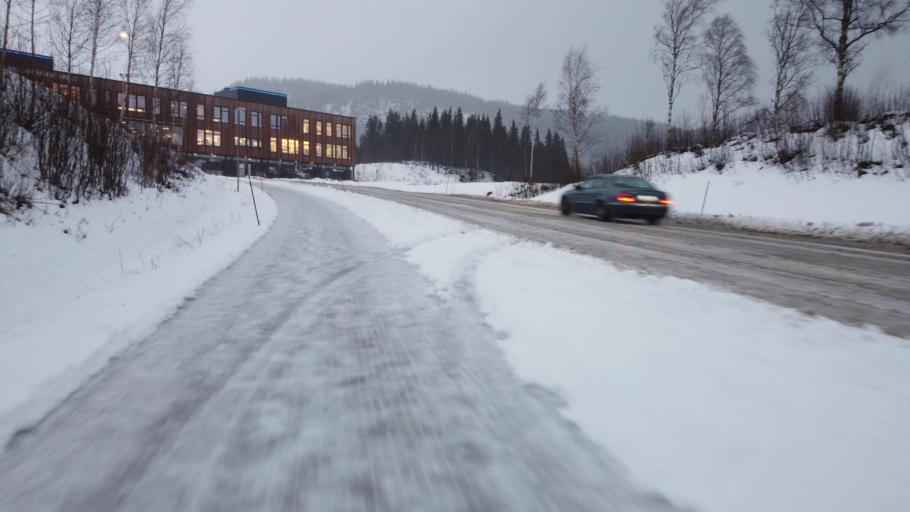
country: NO
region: Nordland
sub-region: Rana
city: Mo i Rana
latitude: 66.3293
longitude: 14.1570
